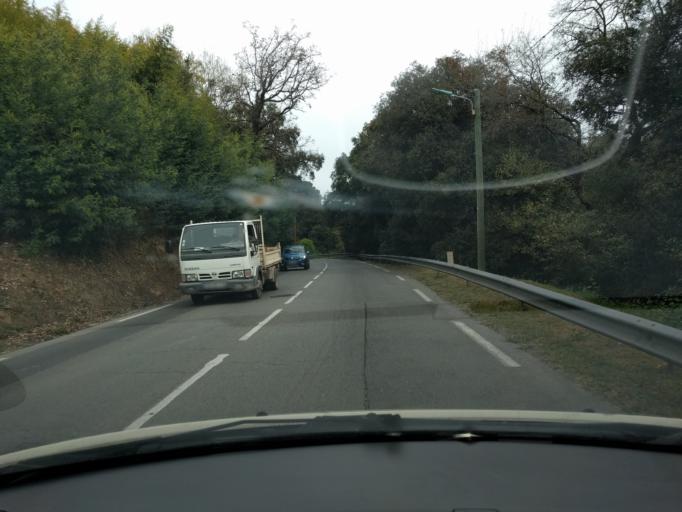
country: FR
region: Provence-Alpes-Cote d'Azur
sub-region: Departement des Alpes-Maritimes
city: La Roquette-sur-Siagne
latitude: 43.5825
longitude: 6.9584
